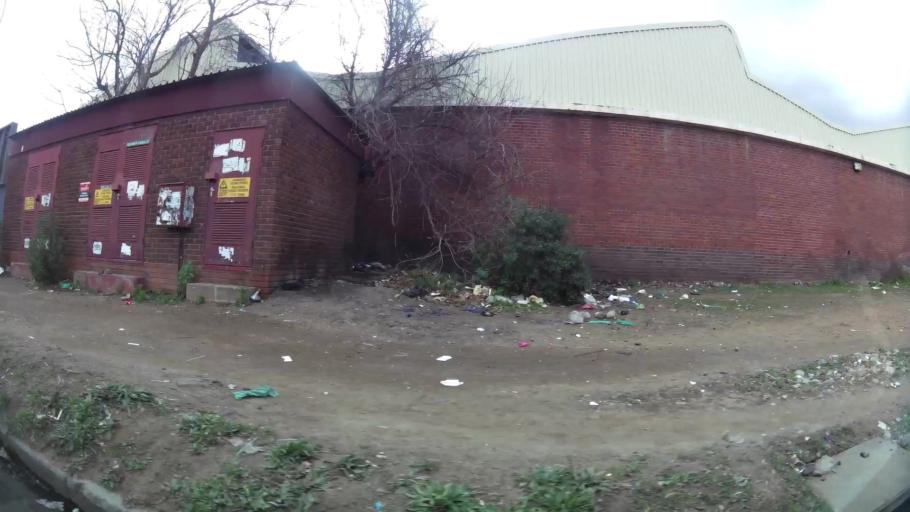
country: ZA
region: Orange Free State
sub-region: Mangaung Metropolitan Municipality
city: Bloemfontein
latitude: -29.1271
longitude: 26.2224
